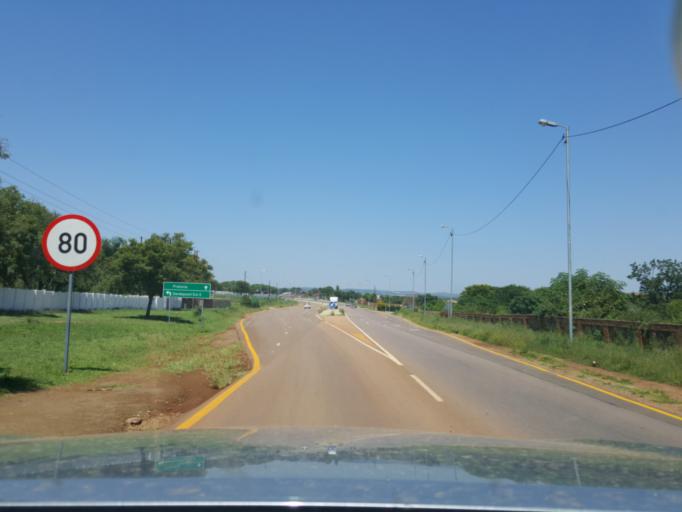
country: ZA
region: Gauteng
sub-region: City of Tshwane Metropolitan Municipality
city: Pretoria
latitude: -25.6787
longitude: 28.3006
